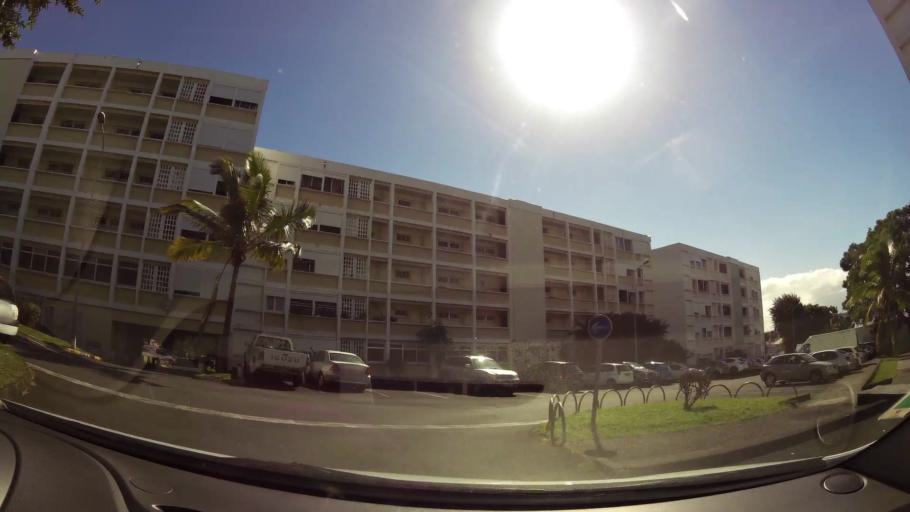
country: RE
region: Reunion
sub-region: Reunion
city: Saint-Denis
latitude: -20.8958
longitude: 55.4879
